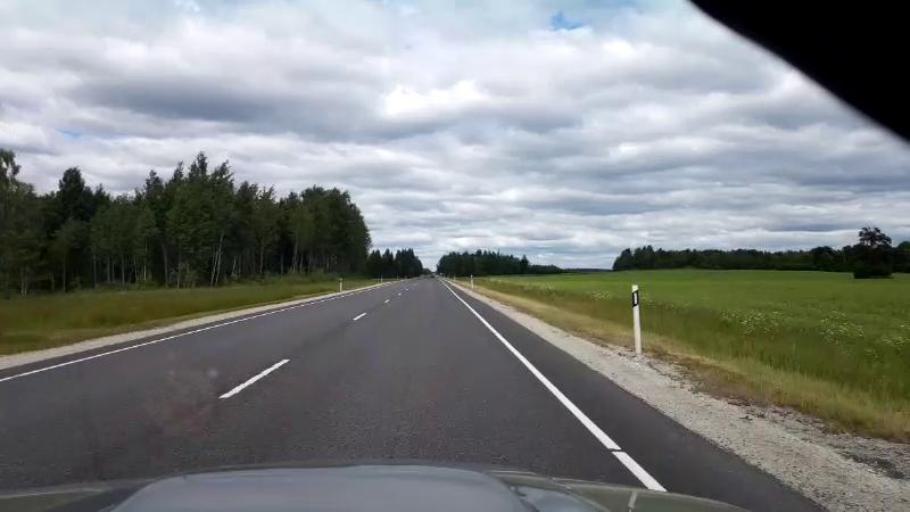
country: EE
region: Raplamaa
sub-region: Maerjamaa vald
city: Marjamaa
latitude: 58.8519
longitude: 24.4310
